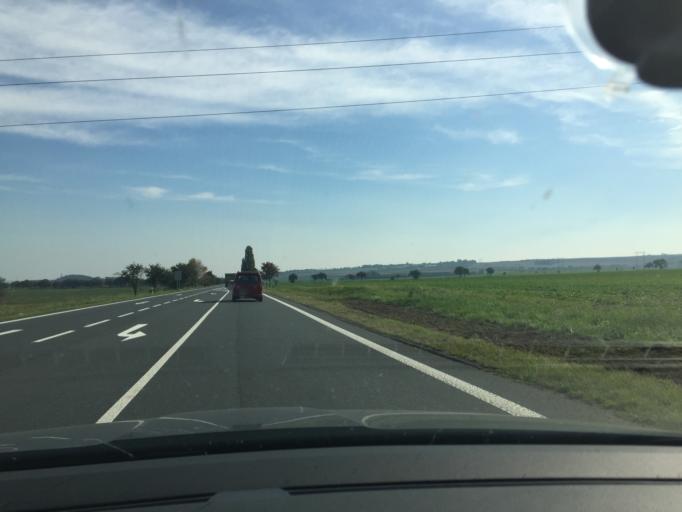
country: CZ
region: Central Bohemia
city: Cerhenice
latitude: 50.0446
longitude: 15.0768
